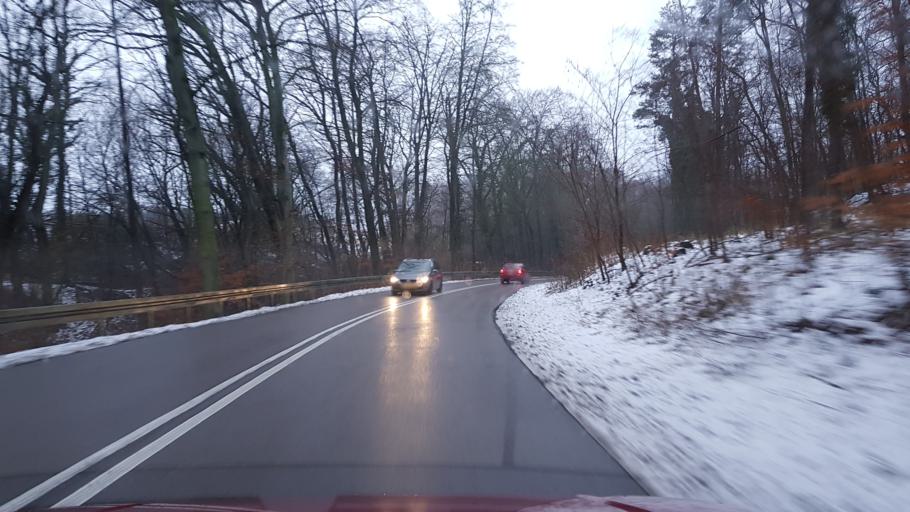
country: PL
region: West Pomeranian Voivodeship
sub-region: Powiat policki
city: Police
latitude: 53.5068
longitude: 14.5032
